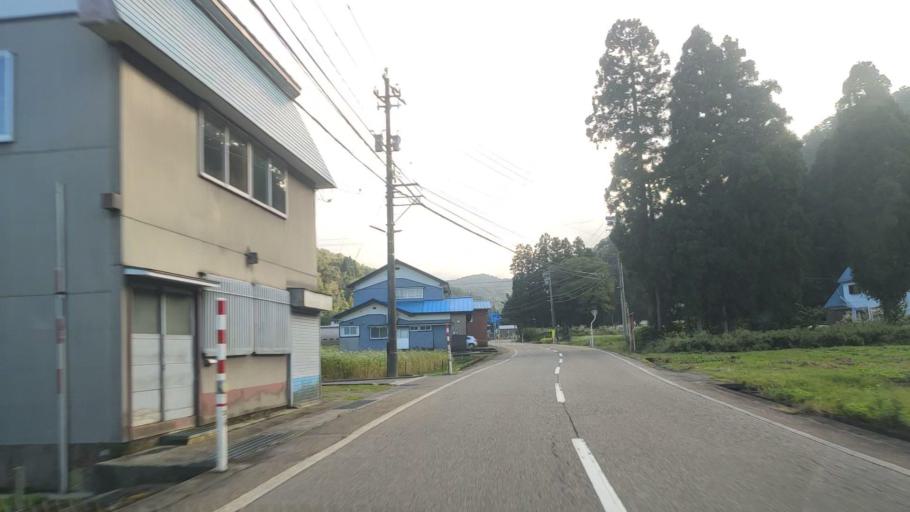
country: JP
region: Toyama
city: Yatsuomachi-higashikumisaka
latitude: 36.4545
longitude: 137.0414
